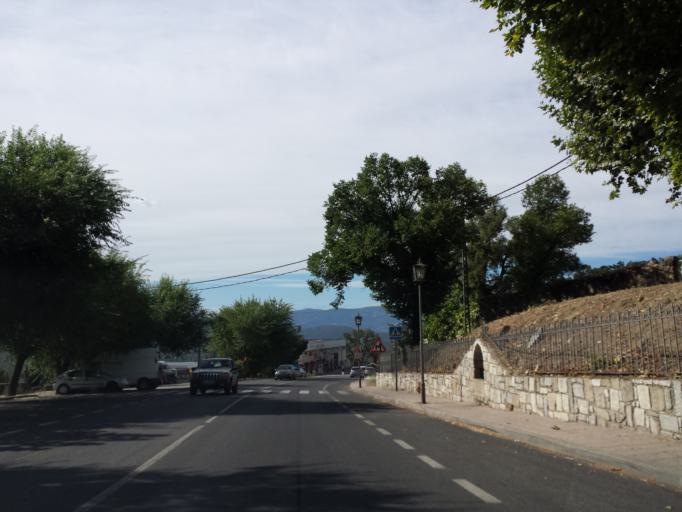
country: ES
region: Castille and Leon
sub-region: Provincia de Avila
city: Piedralaves
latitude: 40.3139
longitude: -4.7025
